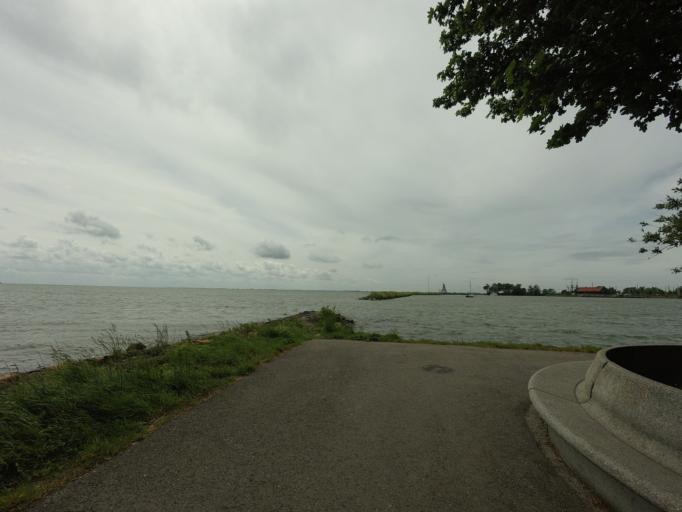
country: NL
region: North Holland
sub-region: Gemeente Hoorn
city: Hoorn
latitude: 52.6350
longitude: 5.0682
